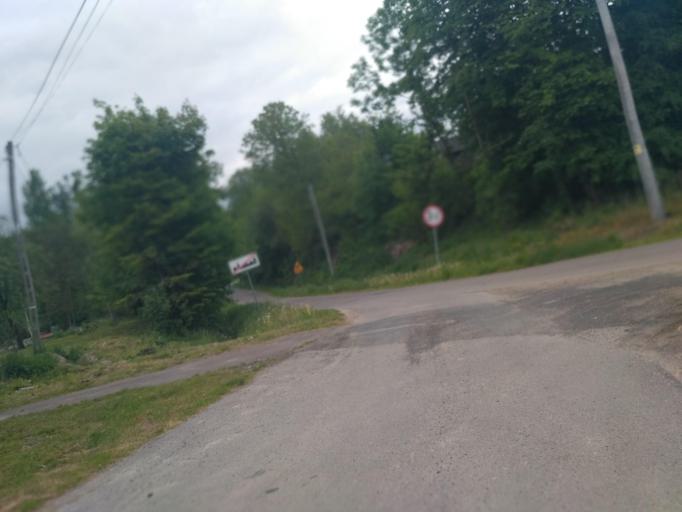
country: PL
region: Subcarpathian Voivodeship
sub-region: Powiat jasielski
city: Tarnowiec
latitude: 49.7072
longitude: 21.5828
